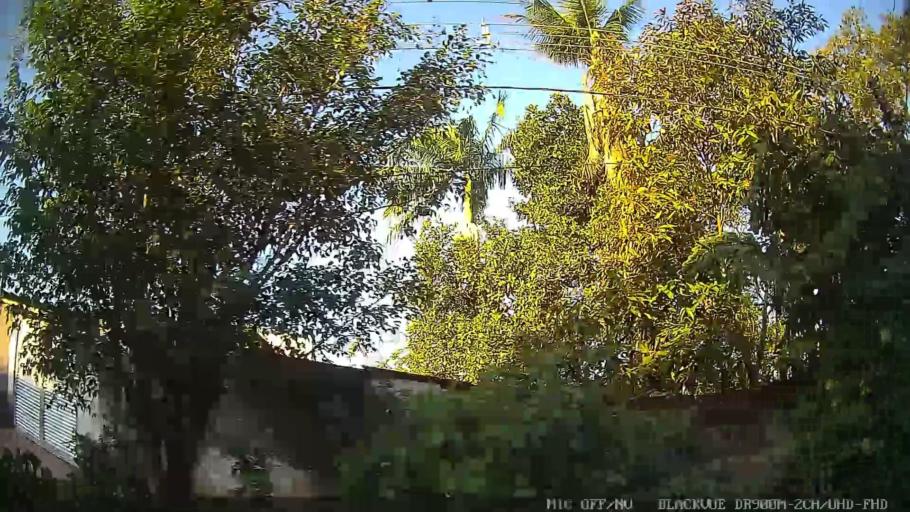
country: BR
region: Sao Paulo
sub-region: Guaruja
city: Guaruja
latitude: -23.9651
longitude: -46.2817
